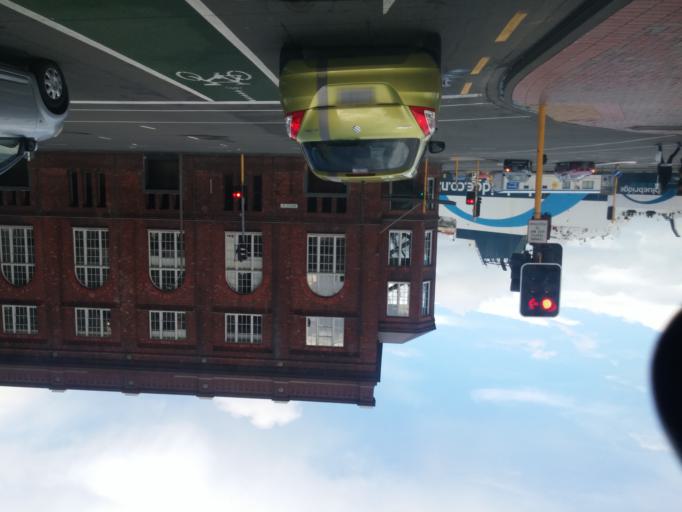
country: NZ
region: Wellington
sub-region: Wellington City
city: Wellington
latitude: -41.2799
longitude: 174.7801
